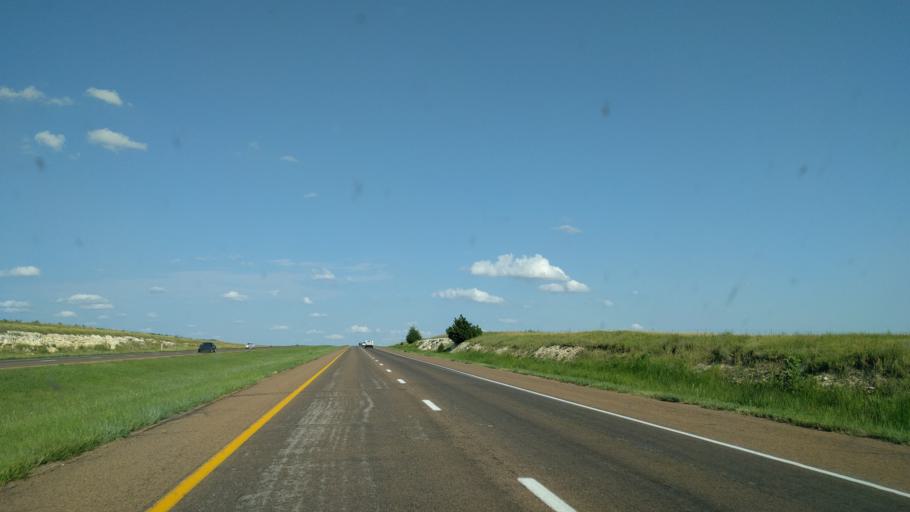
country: US
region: Kansas
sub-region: Ellis County
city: Ellis
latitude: 38.9402
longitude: -99.4906
